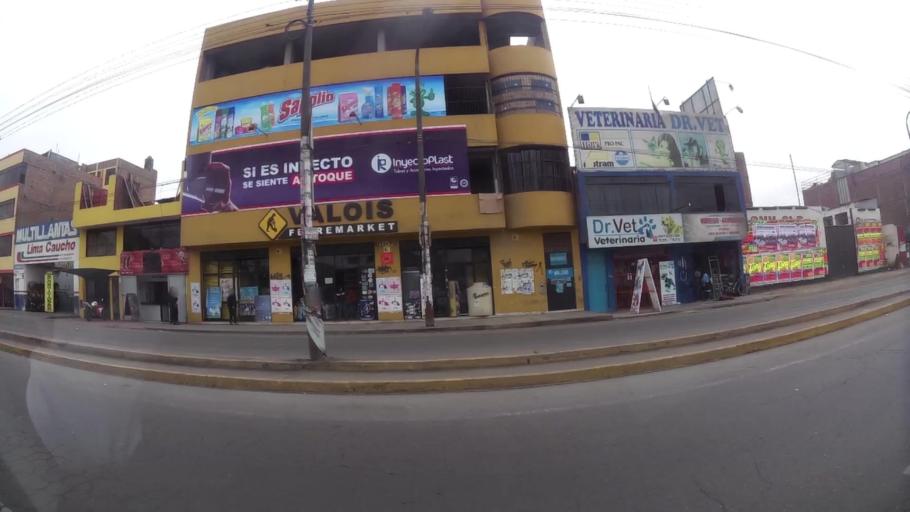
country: PE
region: Lima
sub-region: Lima
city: Independencia
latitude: -11.9975
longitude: -77.0847
